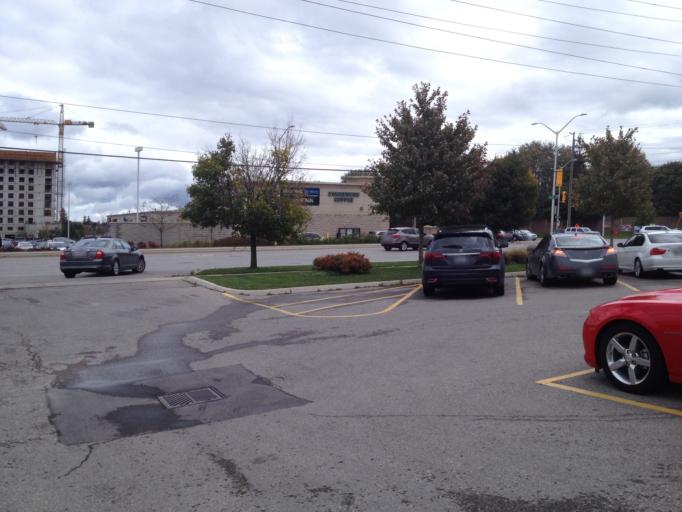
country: CA
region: Ontario
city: London
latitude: 43.0189
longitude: -81.3112
